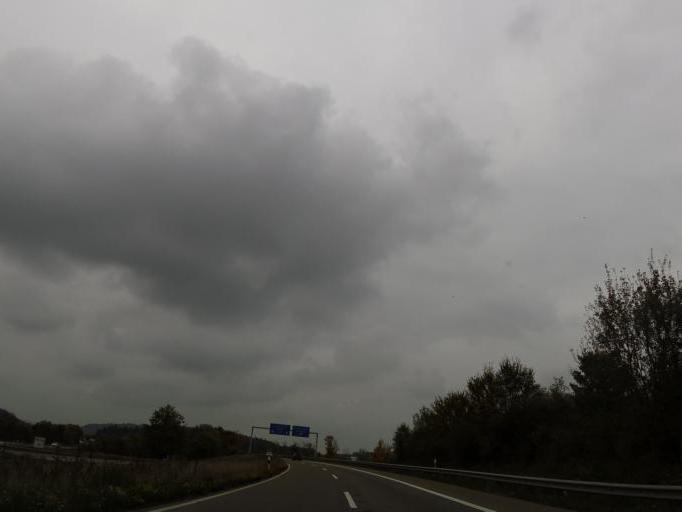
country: DE
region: Rheinland-Pfalz
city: Kaiserslautern
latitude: 49.4611
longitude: 7.7971
